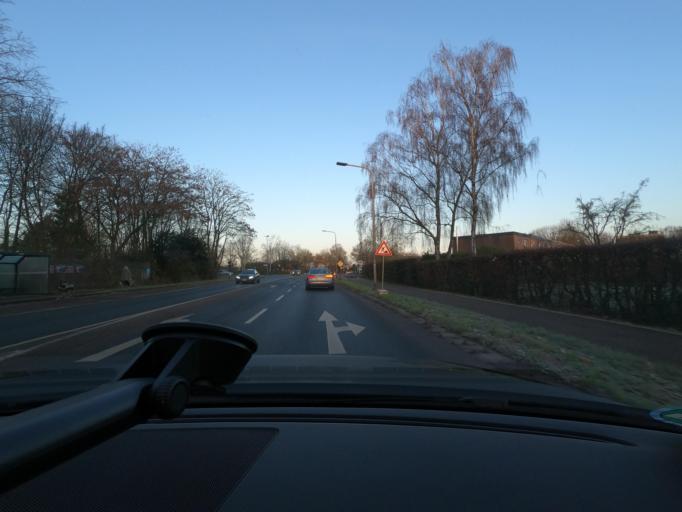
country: DE
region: North Rhine-Westphalia
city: Kempen
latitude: 51.3705
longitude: 6.4065
